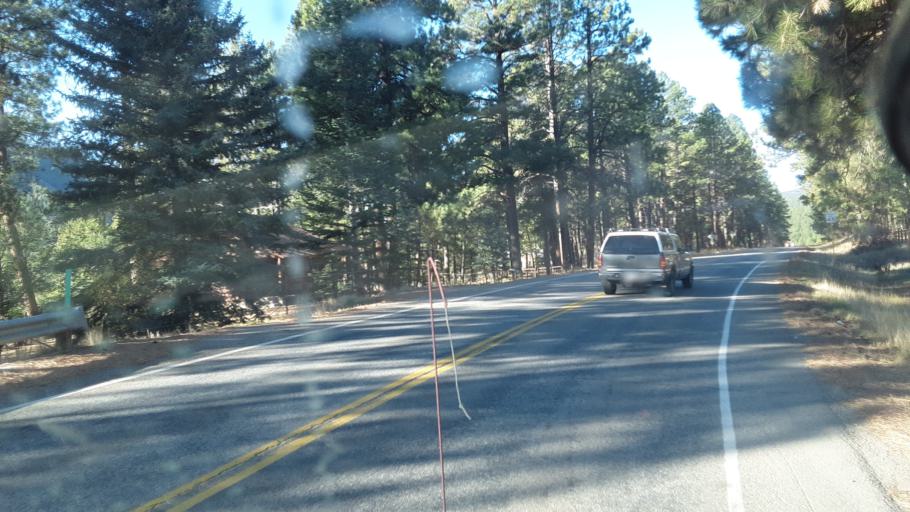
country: US
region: Colorado
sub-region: La Plata County
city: Durango
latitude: 37.3311
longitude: -107.7321
